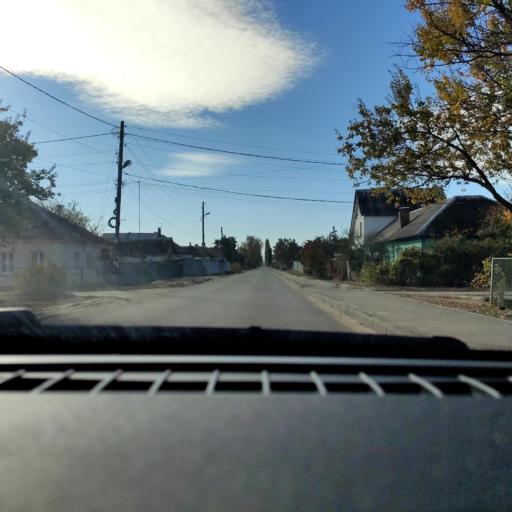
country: RU
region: Voronezj
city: Maslovka
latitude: 51.6090
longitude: 39.2207
